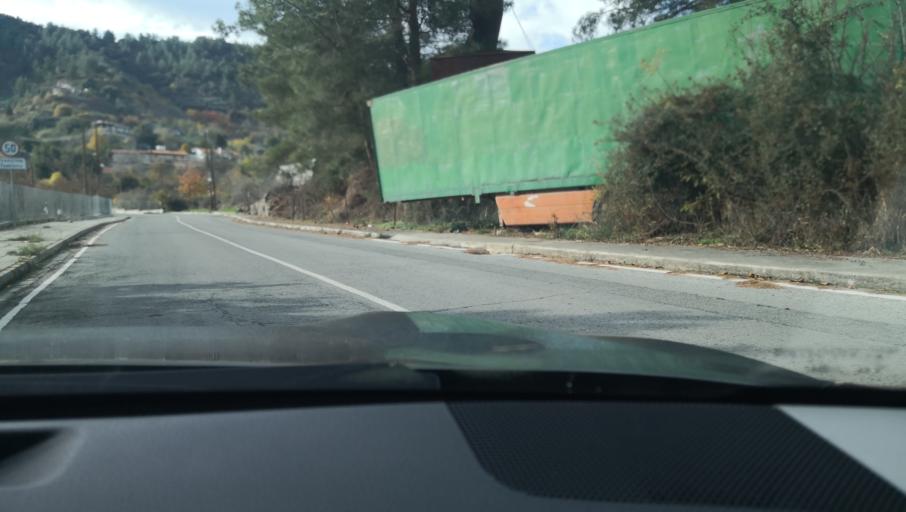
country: CY
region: Lefkosia
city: Lefka
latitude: 35.0259
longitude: 32.7256
